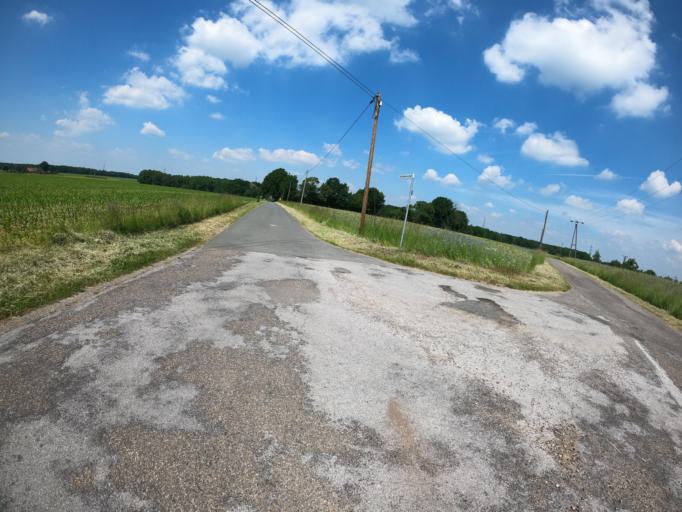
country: DE
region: North Rhine-Westphalia
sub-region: Regierungsbezirk Dusseldorf
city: Hunxe
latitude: 51.7071
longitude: 6.7373
